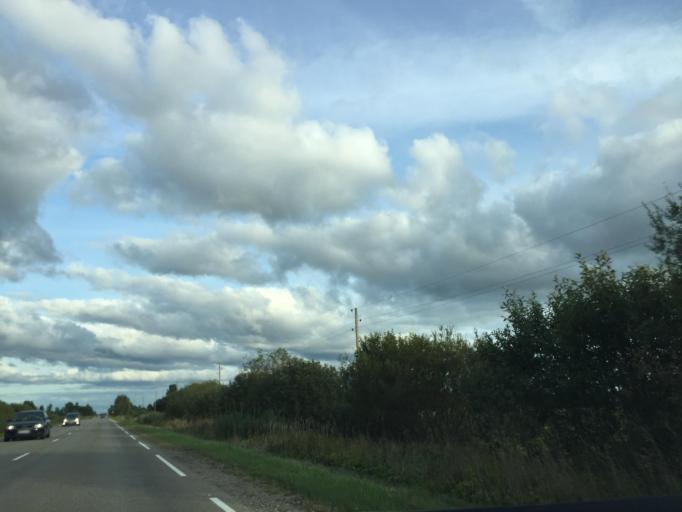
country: LV
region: Nereta
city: Nereta
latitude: 56.2578
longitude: 25.1991
